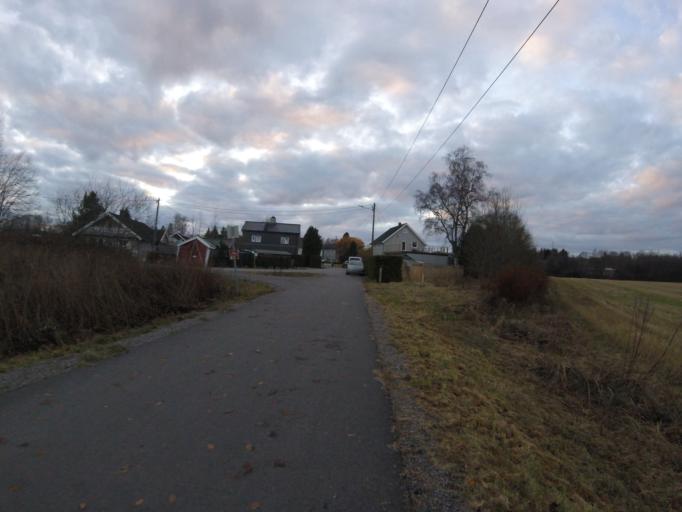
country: NO
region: Akershus
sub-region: Skedsmo
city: Leirsund
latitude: 59.9985
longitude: 11.0911
